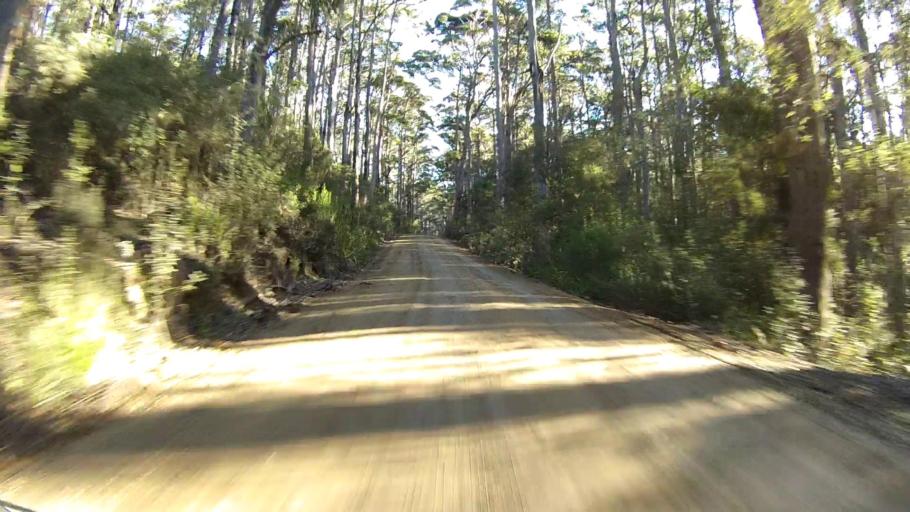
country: AU
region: Tasmania
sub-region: Clarence
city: Sandford
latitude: -43.1448
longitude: 147.9443
